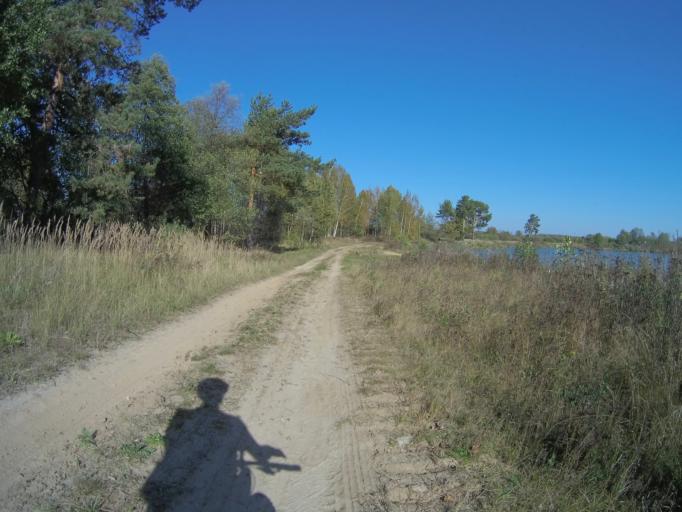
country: RU
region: Vladimir
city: Raduzhnyy
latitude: 56.0316
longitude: 40.3251
